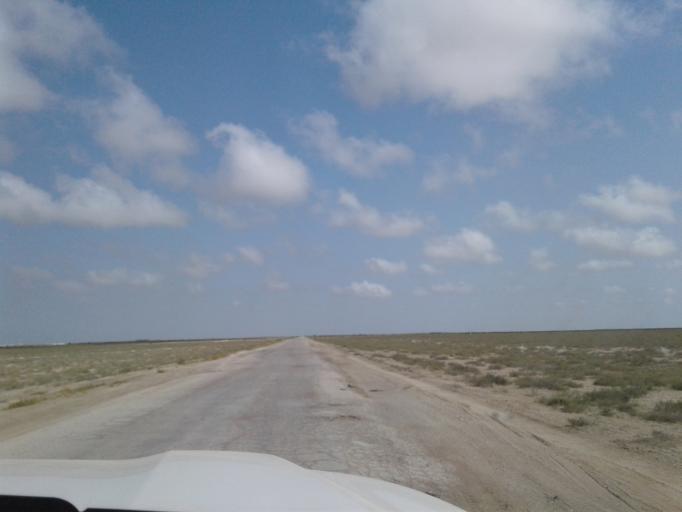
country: IR
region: Golestan
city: Gomishan
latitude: 37.6175
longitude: 53.9268
